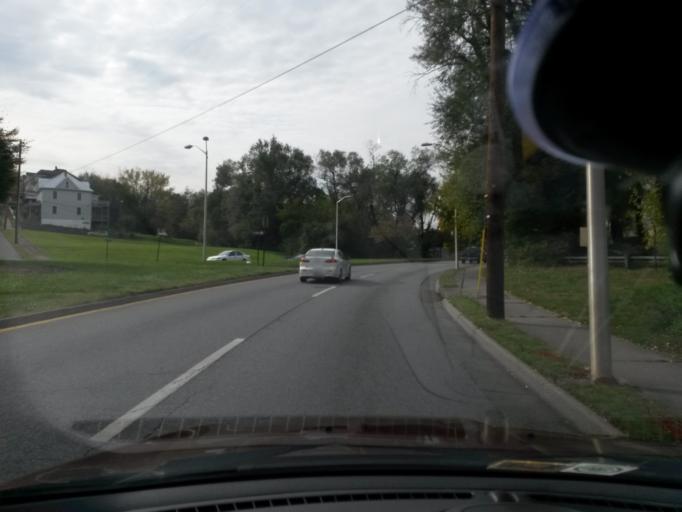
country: US
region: Virginia
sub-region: City of Roanoke
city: Cedar Bluff
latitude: 37.2677
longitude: -79.9330
